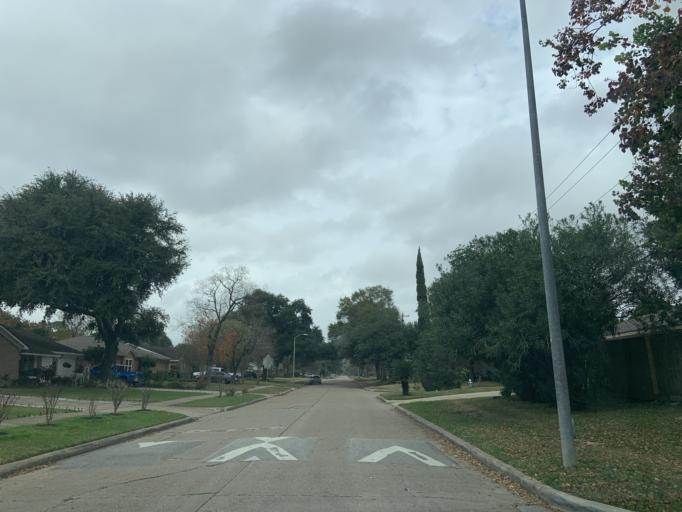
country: US
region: Texas
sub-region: Harris County
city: Bellaire
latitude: 29.6852
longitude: -95.5176
